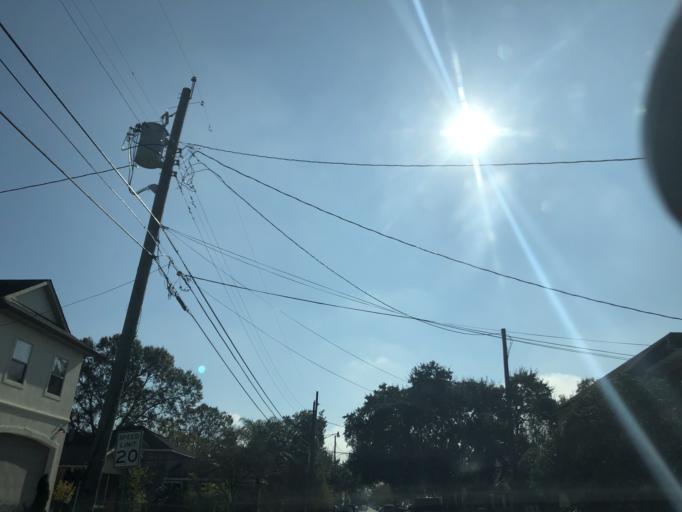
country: US
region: Louisiana
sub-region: Jefferson Parish
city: Metairie
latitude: 29.9898
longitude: -90.1518
